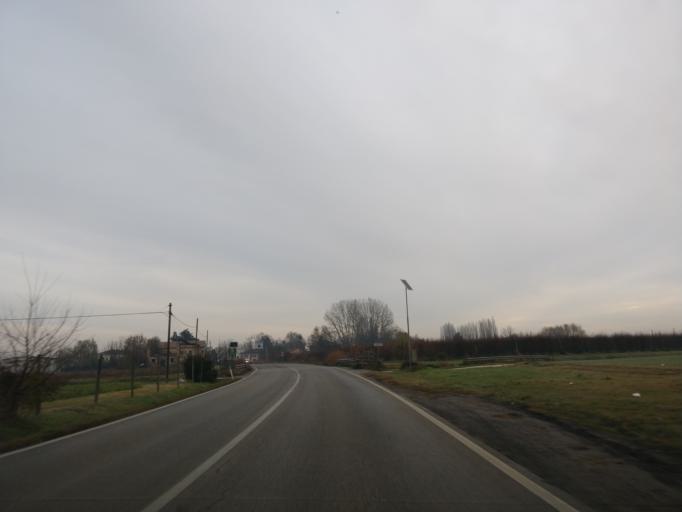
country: IT
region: Emilia-Romagna
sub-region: Provincia di Ferrara
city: Dosso
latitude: 44.7669
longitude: 11.3228
